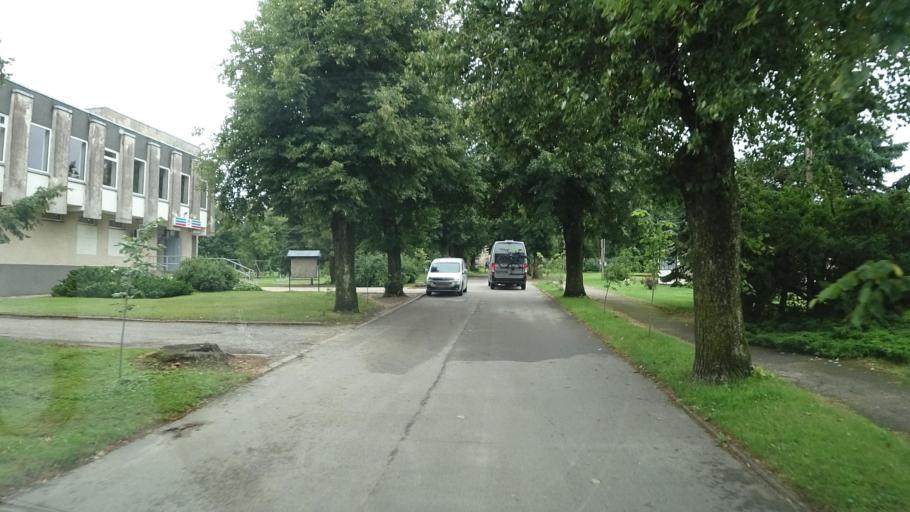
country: LT
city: Ramygala
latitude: 55.4211
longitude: 24.2385
